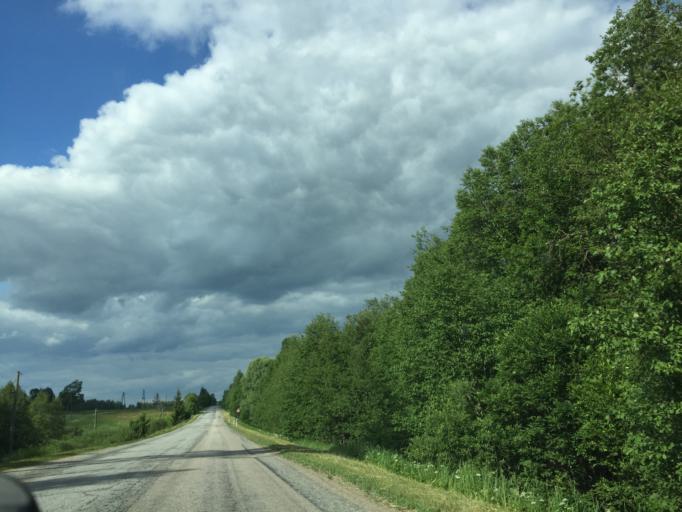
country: LV
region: Skriveri
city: Skriveri
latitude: 56.8144
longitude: 25.1163
